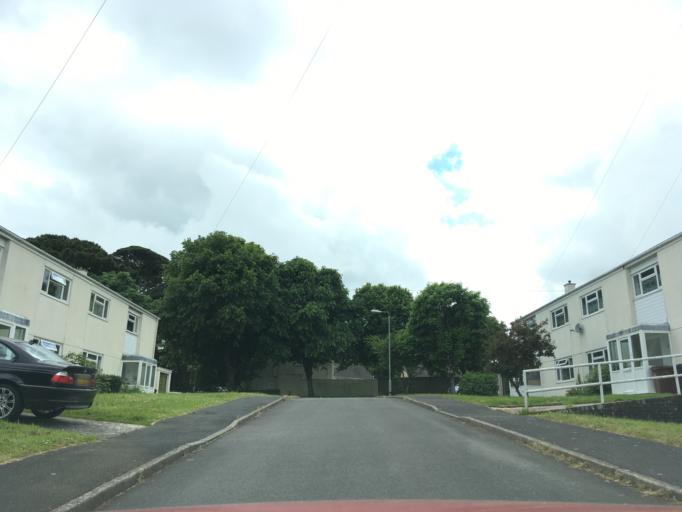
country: GB
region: England
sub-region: Devon
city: Dartmouth
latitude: 50.3541
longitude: -3.5907
